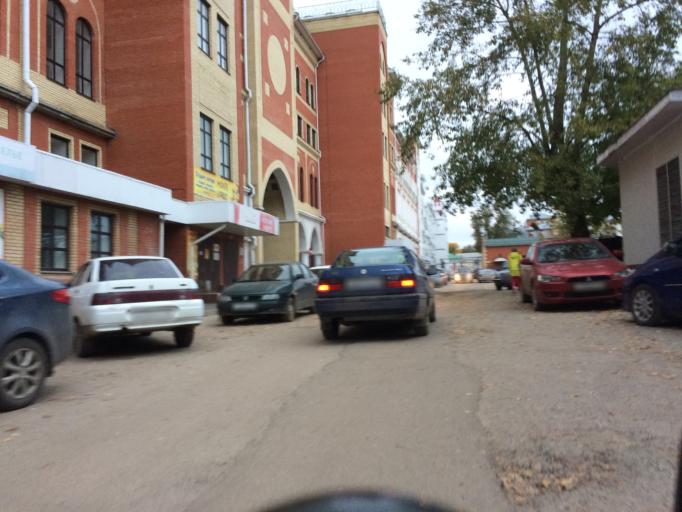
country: RU
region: Mariy-El
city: Yoshkar-Ola
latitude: 56.6318
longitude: 47.8883
